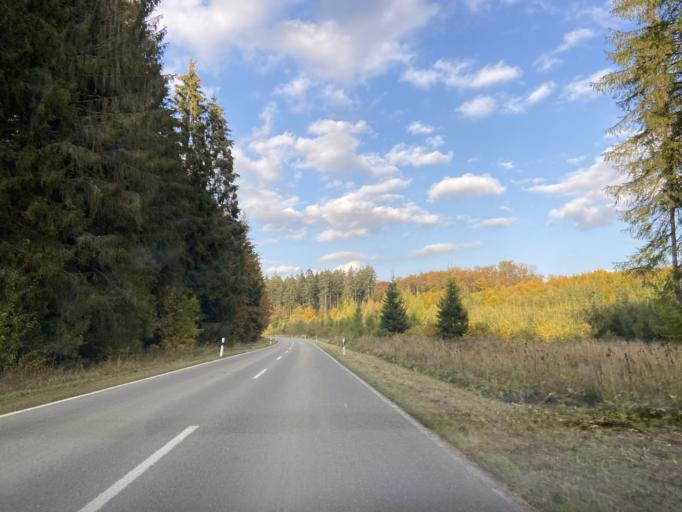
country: DE
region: Baden-Wuerttemberg
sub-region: Tuebingen Region
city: Langenenslingen
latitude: 48.1112
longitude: 9.3384
